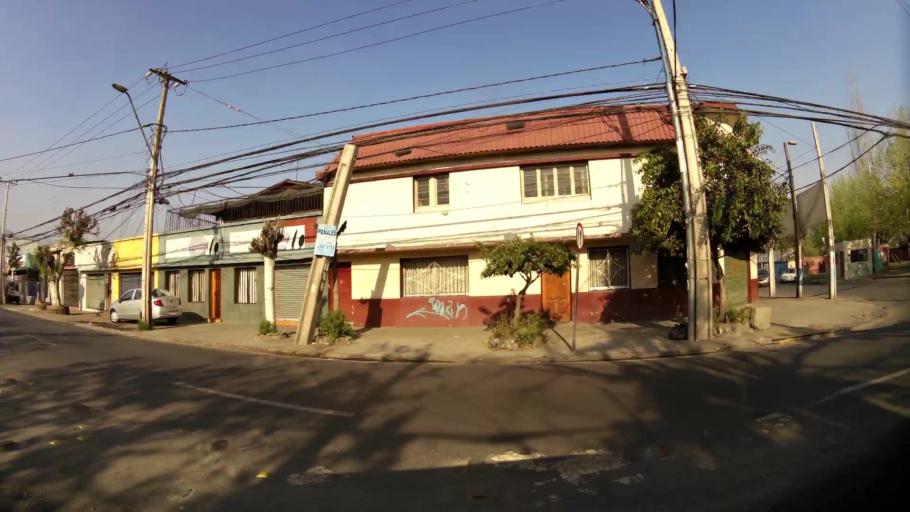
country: CL
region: Santiago Metropolitan
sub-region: Provincia de Santiago
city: Santiago
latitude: -33.3962
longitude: -70.6263
